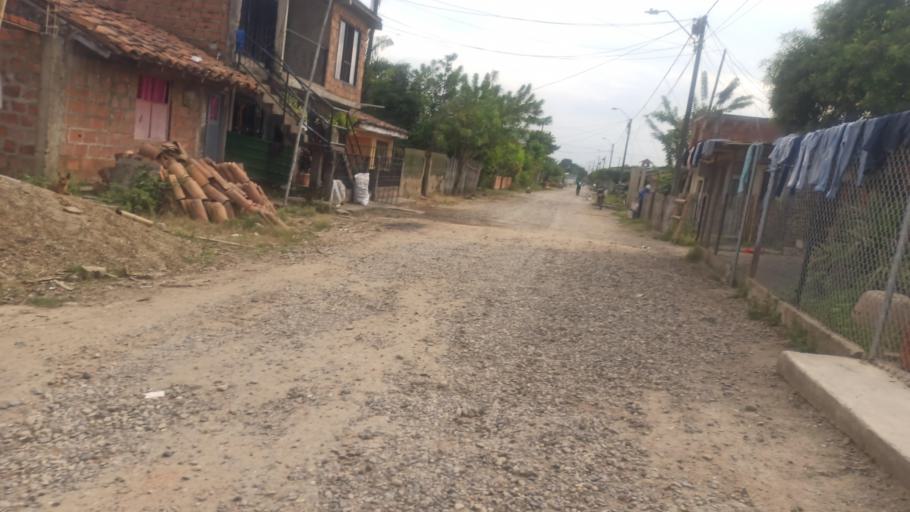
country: CO
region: Valle del Cauca
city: Jamundi
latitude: 3.1281
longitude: -76.5596
